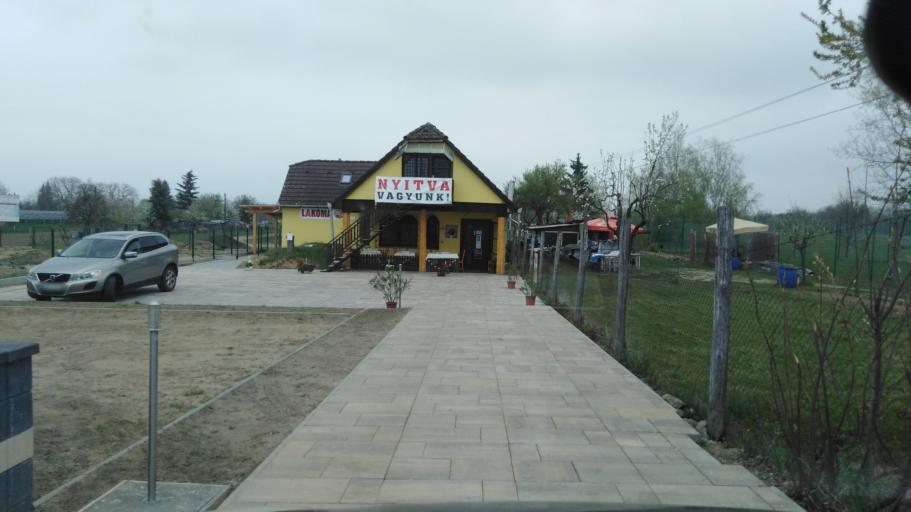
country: HU
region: Nograd
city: Balassagyarmat
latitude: 48.0565
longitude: 19.3094
